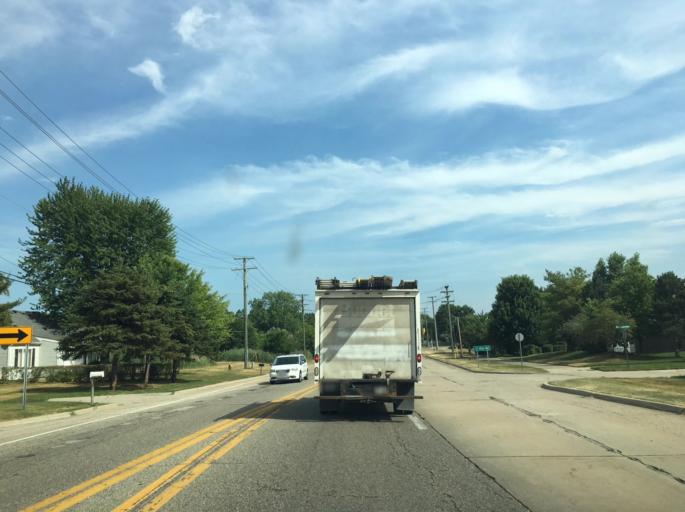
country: US
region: Michigan
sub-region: Macomb County
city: Sterling Heights
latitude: 42.5831
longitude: -82.9970
